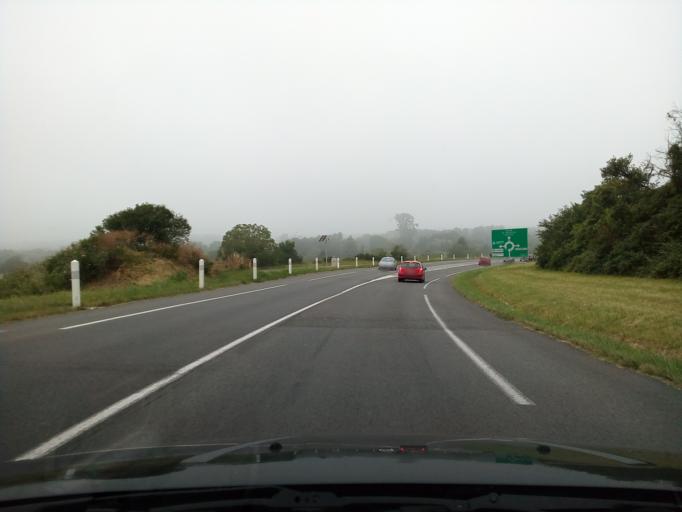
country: FR
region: Poitou-Charentes
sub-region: Departement de la Charente-Maritime
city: Cherac
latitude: 45.6895
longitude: -0.3929
